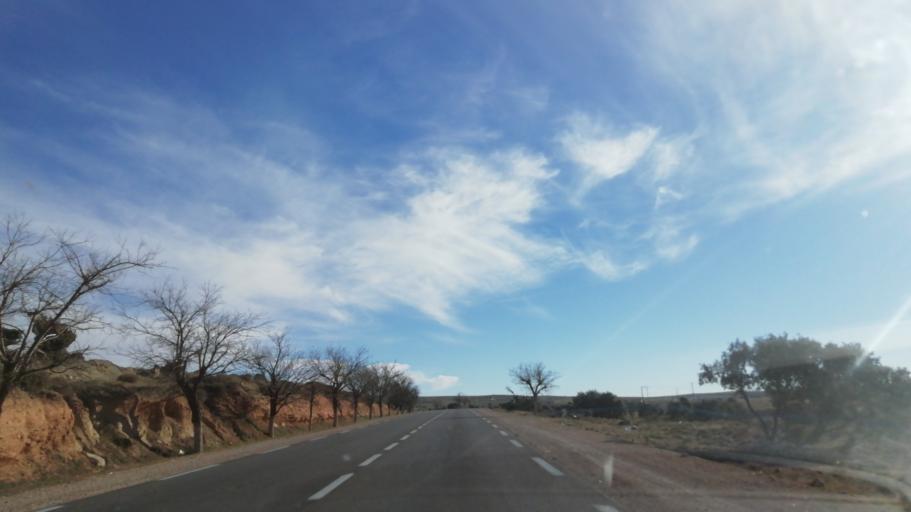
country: DZ
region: Tlemcen
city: Sebdou
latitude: 34.5687
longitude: -1.3190
